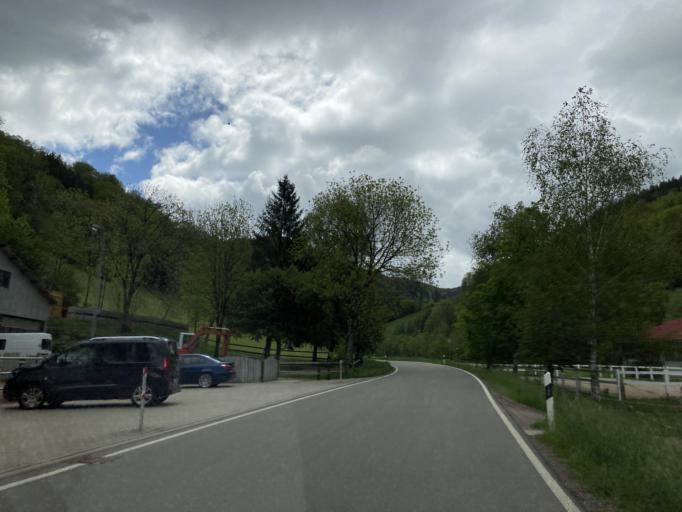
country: DE
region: Baden-Wuerttemberg
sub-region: Freiburg Region
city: Muhlenbach
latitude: 48.2083
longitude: 8.1548
